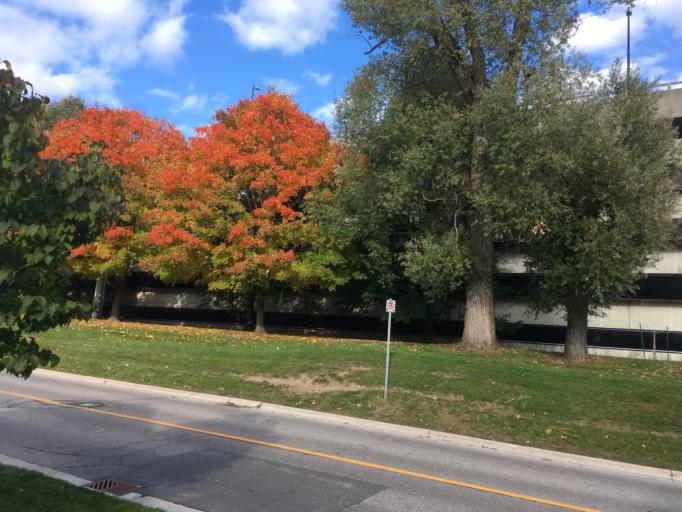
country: CA
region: Ontario
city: Oshawa
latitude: 43.9038
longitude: -78.8700
